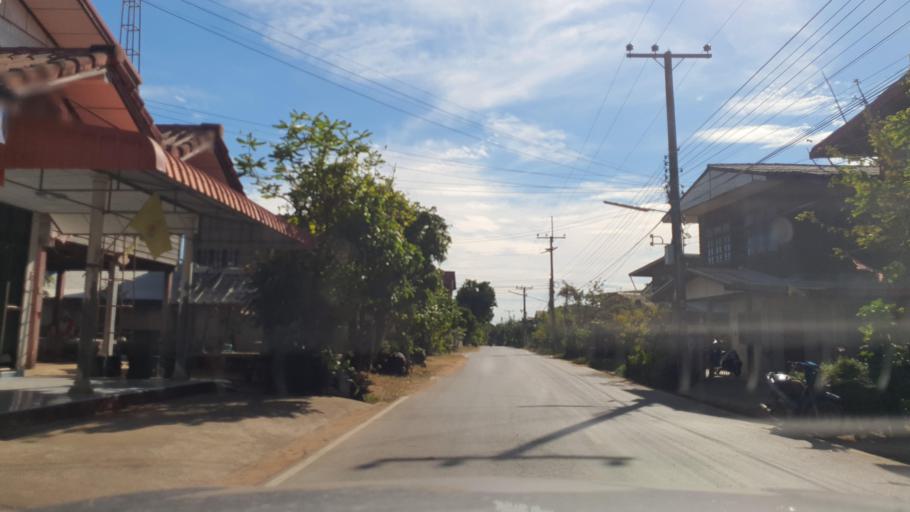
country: TH
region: Kalasin
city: Kuchinarai
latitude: 16.5913
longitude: 104.1314
